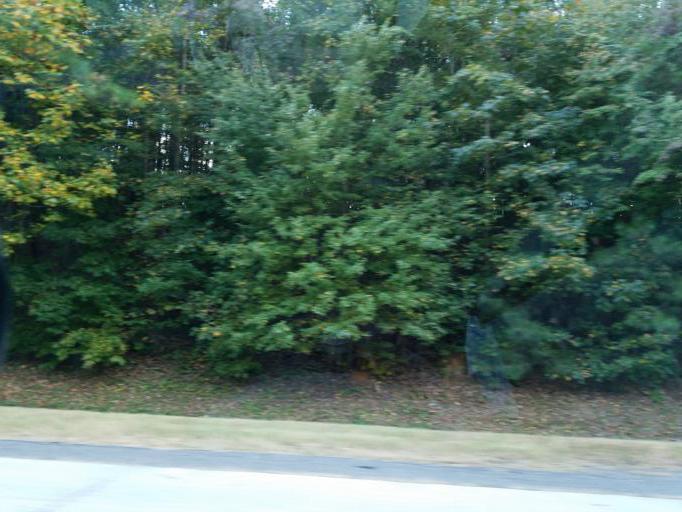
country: US
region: Georgia
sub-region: Cobb County
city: Kennesaw
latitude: 34.0758
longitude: -84.6225
